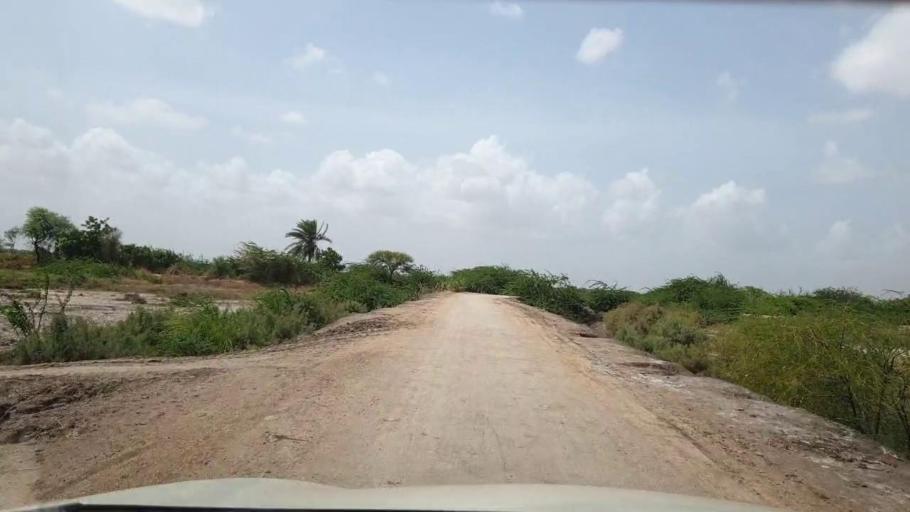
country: PK
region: Sindh
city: Kadhan
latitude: 24.4229
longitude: 68.8322
